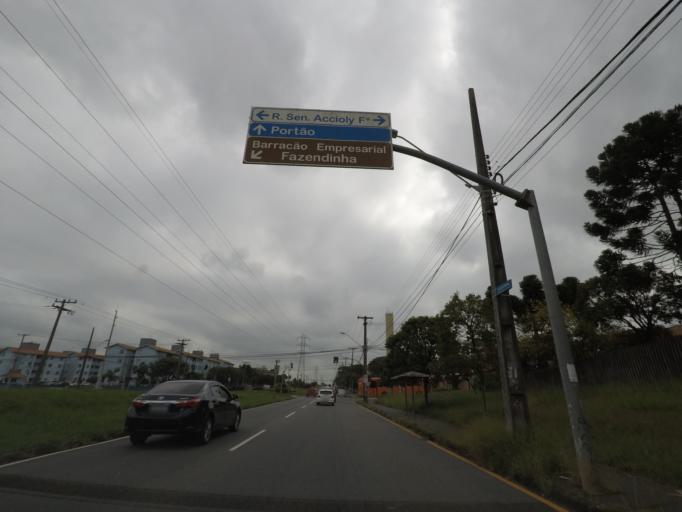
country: BR
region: Parana
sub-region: Curitiba
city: Curitiba
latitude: -25.4977
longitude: -49.3181
